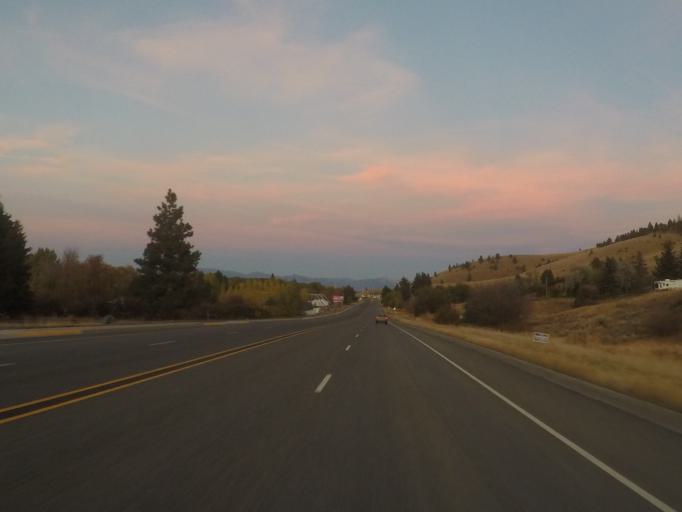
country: US
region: Montana
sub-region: Lewis and Clark County
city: Helena West Side
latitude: 46.5993
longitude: -112.0994
